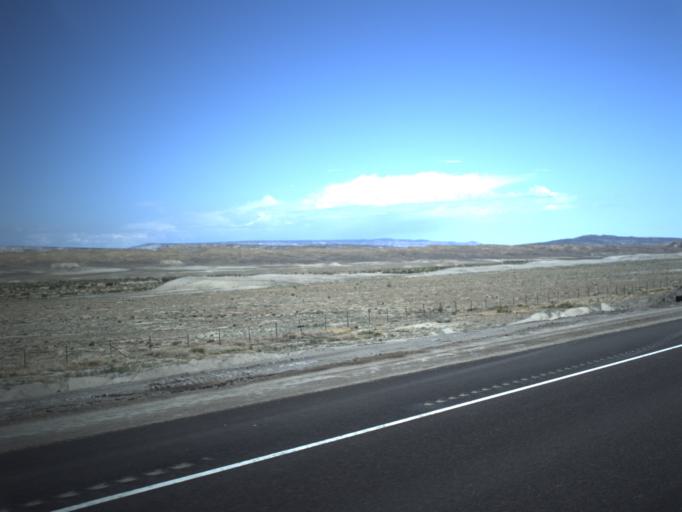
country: US
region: Utah
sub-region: Carbon County
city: East Carbon City
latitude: 39.0384
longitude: -110.3070
